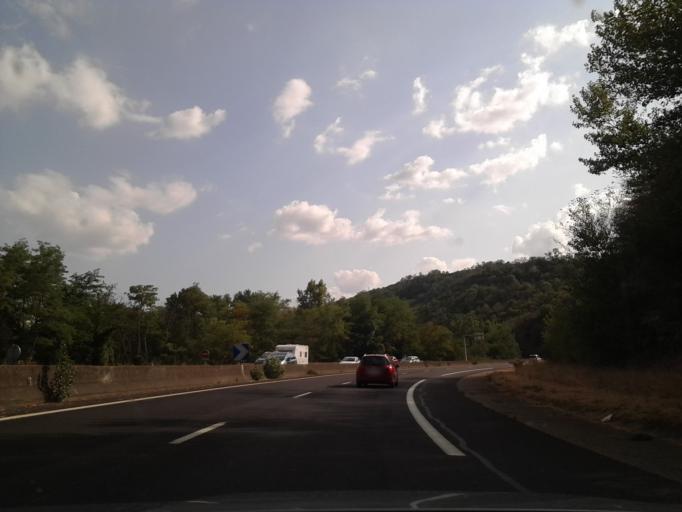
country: FR
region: Auvergne
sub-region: Departement du Puy-de-Dome
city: Vic-le-Comte
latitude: 45.6069
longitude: 3.2210
